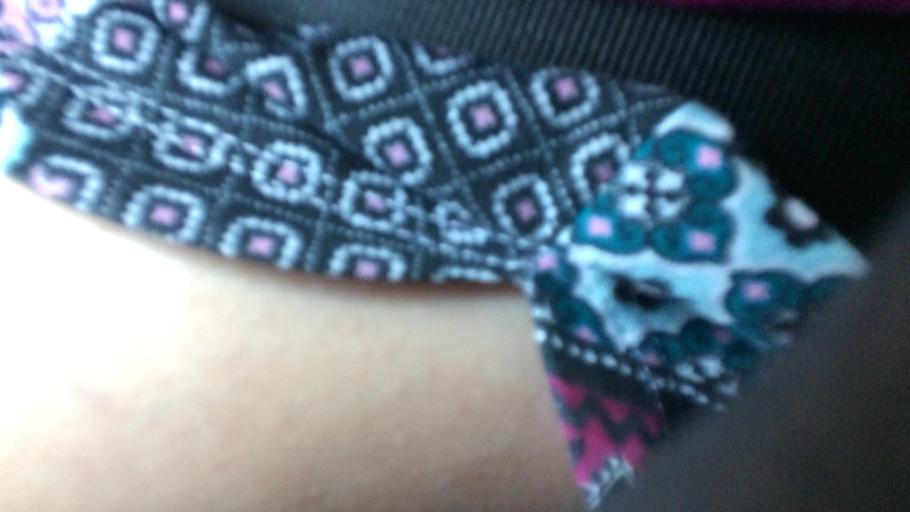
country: US
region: New Mexico
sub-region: Colfax County
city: Springer
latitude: 35.9766
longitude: -104.7449
